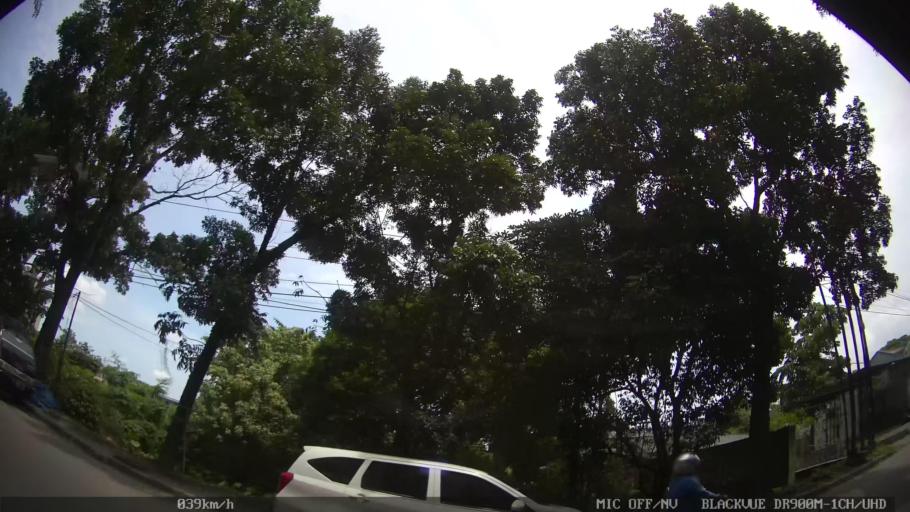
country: ID
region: North Sumatra
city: Sunggal
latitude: 3.5409
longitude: 98.6349
